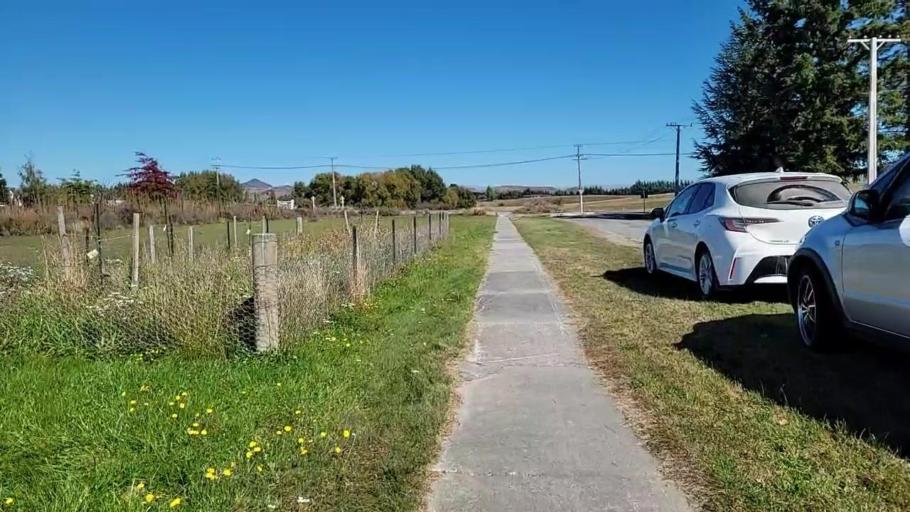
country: NZ
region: Otago
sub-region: Queenstown-Lakes District
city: Wanaka
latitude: -45.0916
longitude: 169.6030
